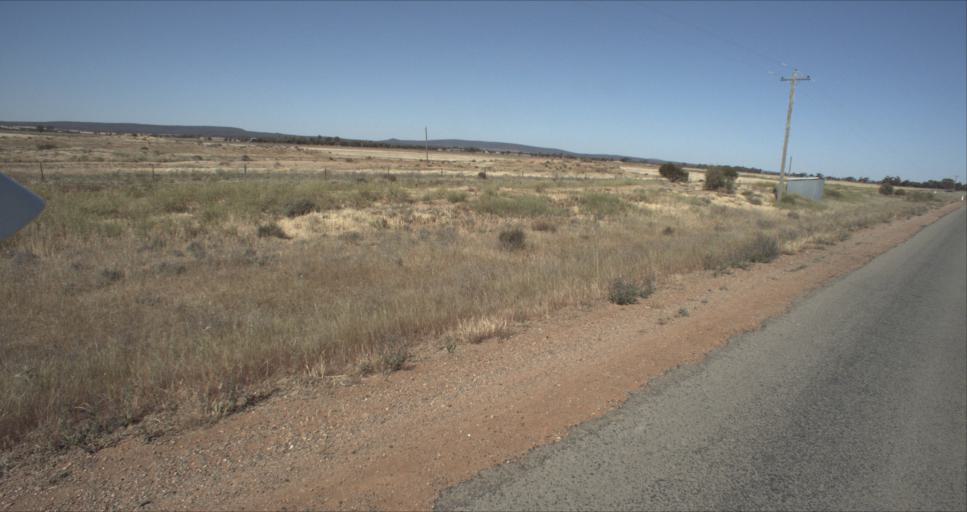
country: AU
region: New South Wales
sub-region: Leeton
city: Leeton
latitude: -34.4914
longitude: 146.3838
